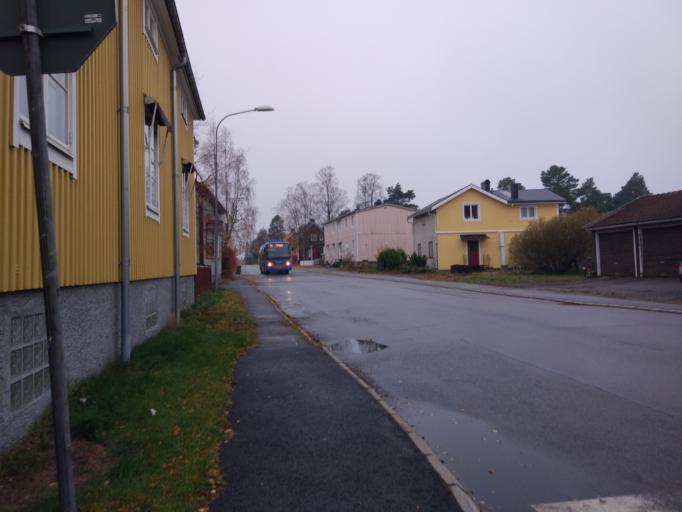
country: SE
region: Vaesterbotten
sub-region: Umea Kommun
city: Holmsund
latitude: 63.7021
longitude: 20.3683
